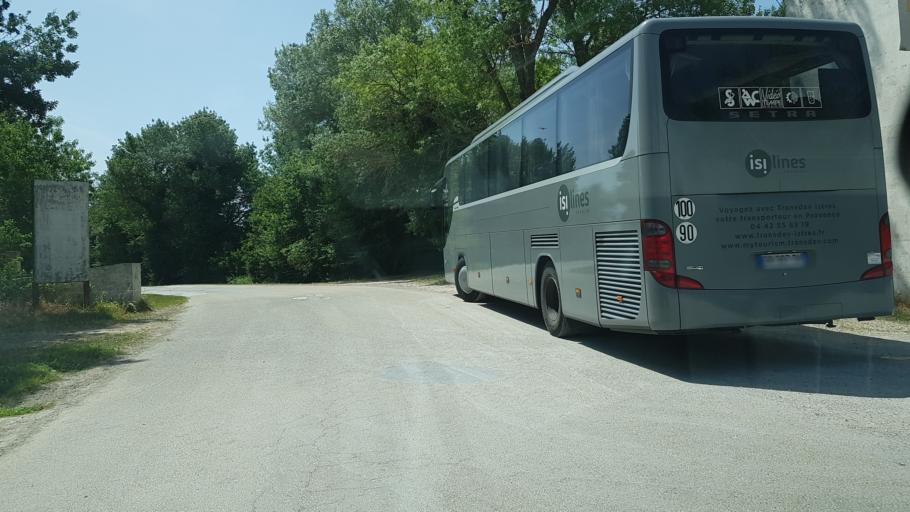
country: FR
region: Languedoc-Roussillon
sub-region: Departement du Gard
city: Saint-Gilles
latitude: 43.5732
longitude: 4.5040
